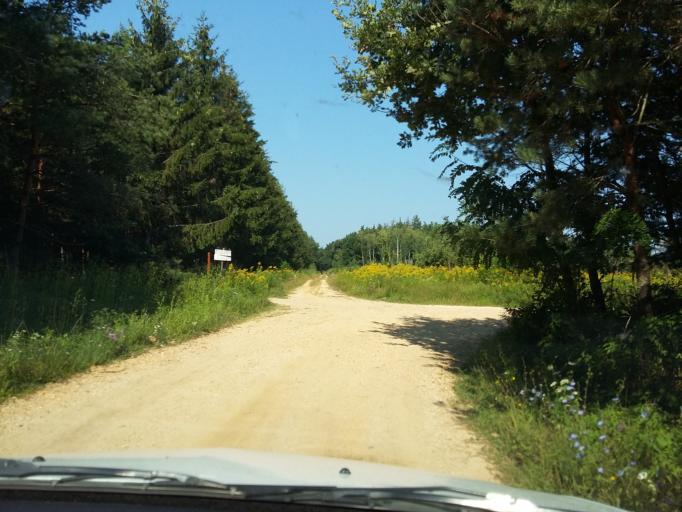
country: SI
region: Hodos-Hodos
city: Hodos
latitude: 46.8577
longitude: 16.3184
